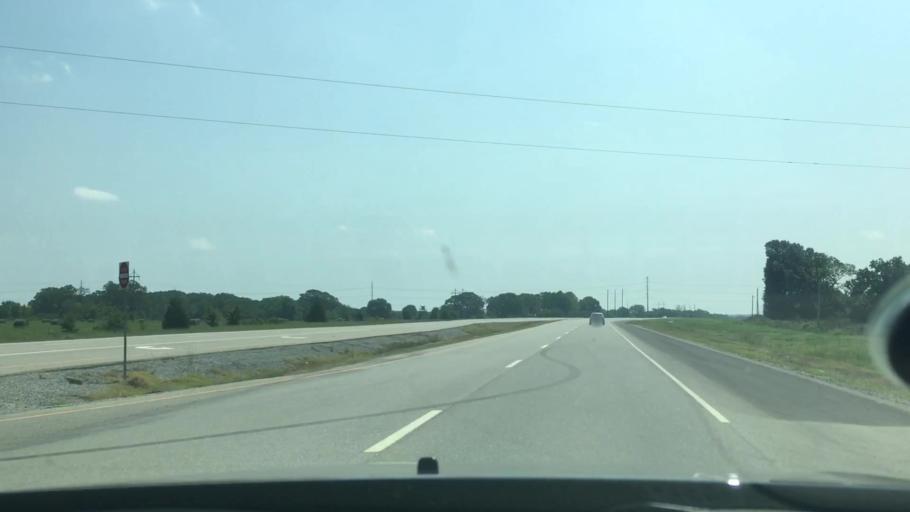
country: US
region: Oklahoma
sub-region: Atoka County
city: Atoka
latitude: 34.3363
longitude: -96.0583
